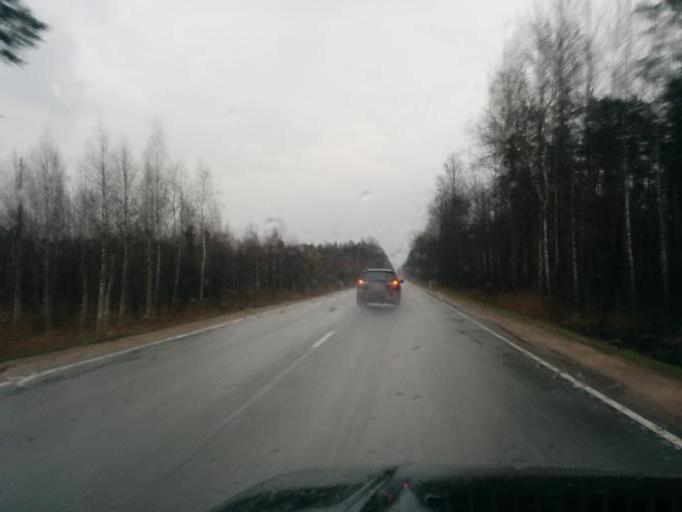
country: LV
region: Kekava
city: Balozi
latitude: 56.8182
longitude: 24.1119
